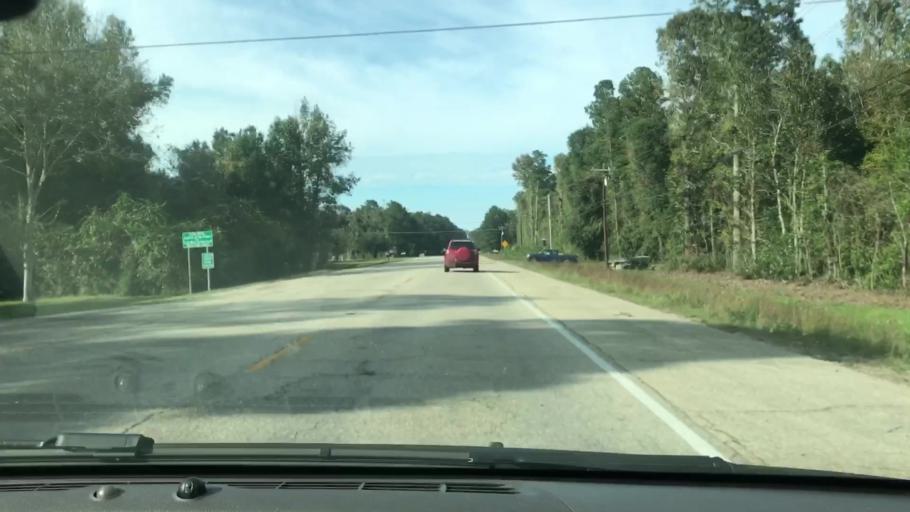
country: US
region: Mississippi
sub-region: Pearl River County
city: Nicholson
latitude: 30.4925
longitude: -89.8115
